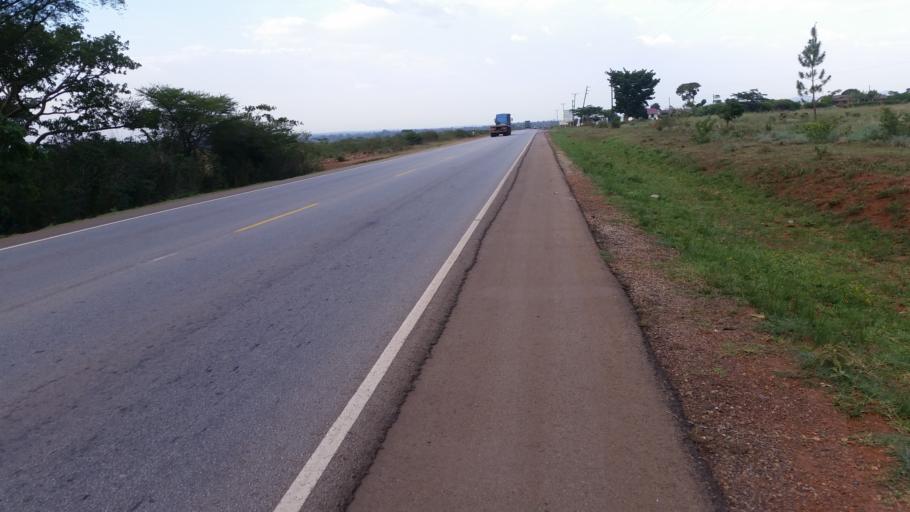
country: UG
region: Eastern Region
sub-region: Busia District
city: Busia
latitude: 0.5481
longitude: 34.0184
